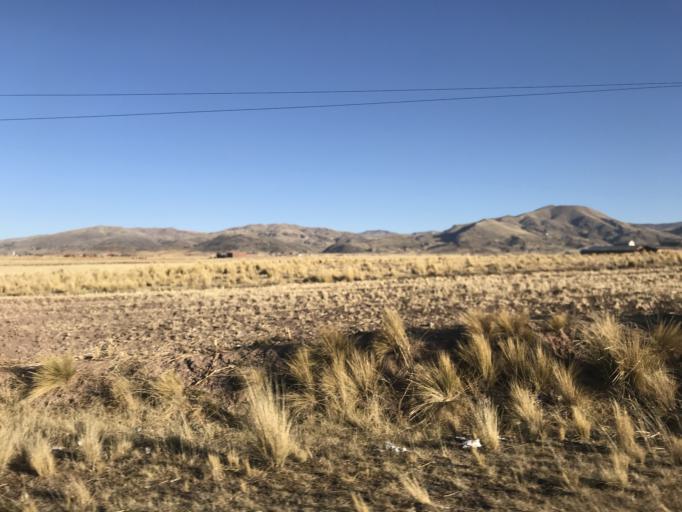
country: BO
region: La Paz
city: Tiahuanaco
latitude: -16.5682
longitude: -68.6563
